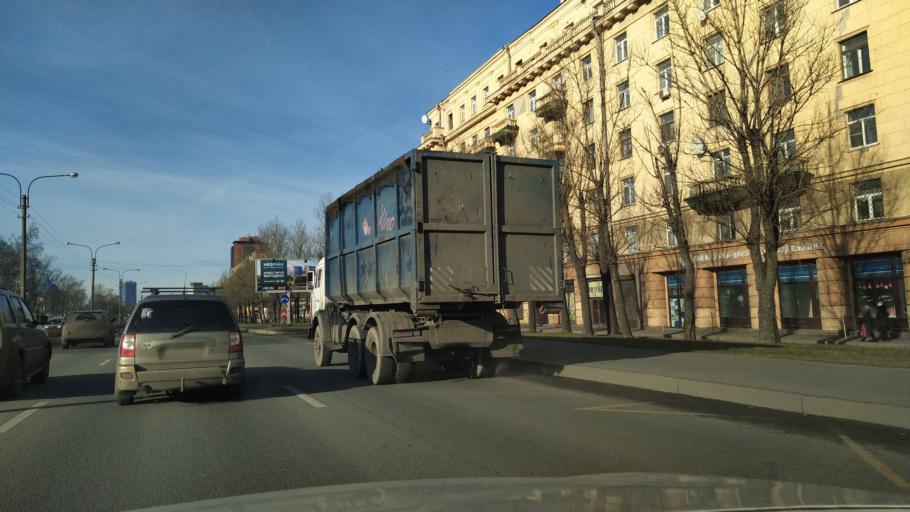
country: RU
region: St.-Petersburg
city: Kupchino
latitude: 59.8342
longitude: 30.3382
